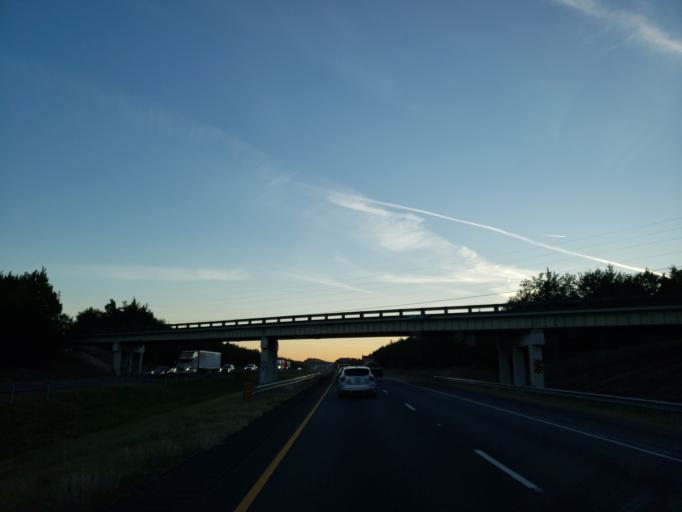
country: US
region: Alabama
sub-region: Sumter County
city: Livingston
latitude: 32.6814
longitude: -88.1637
